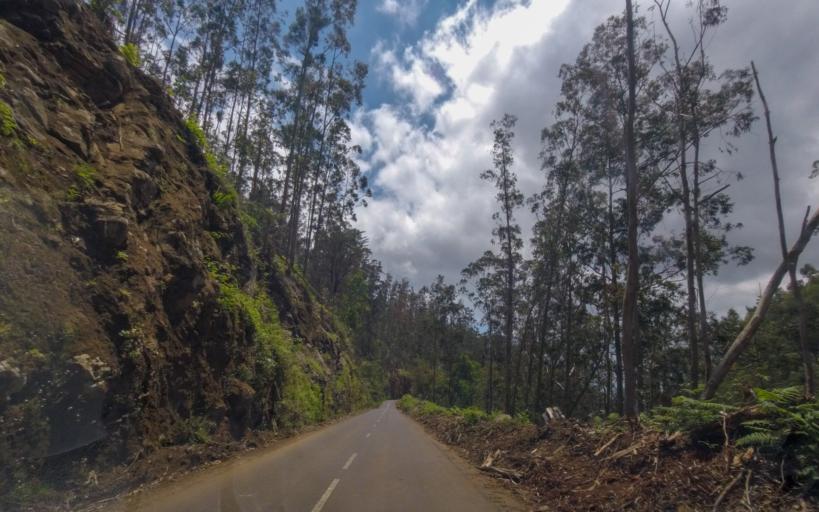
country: PT
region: Madeira
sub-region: Funchal
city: Nossa Senhora do Monte
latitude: 32.6797
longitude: -16.8801
